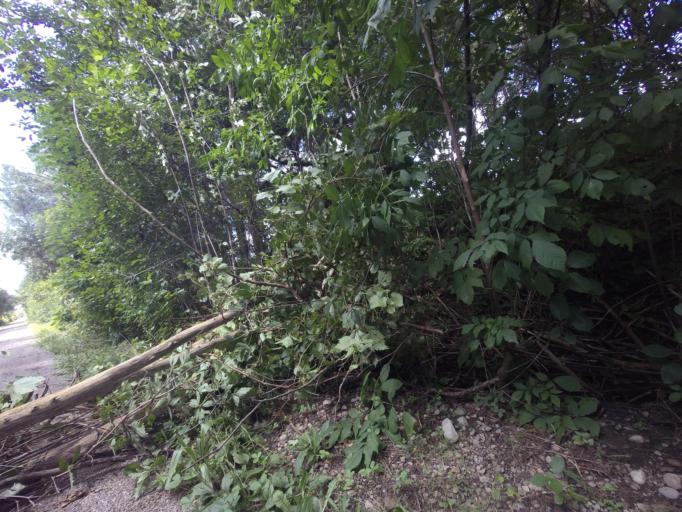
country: CA
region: Ontario
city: Huron East
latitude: 43.6549
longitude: -81.2380
